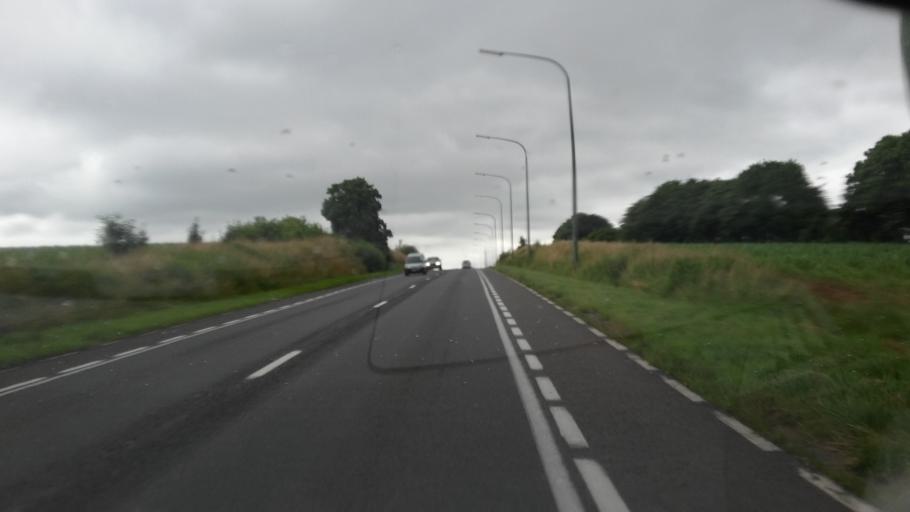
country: BE
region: Wallonia
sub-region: Province du Luxembourg
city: Arlon
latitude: 49.6633
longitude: 5.8231
